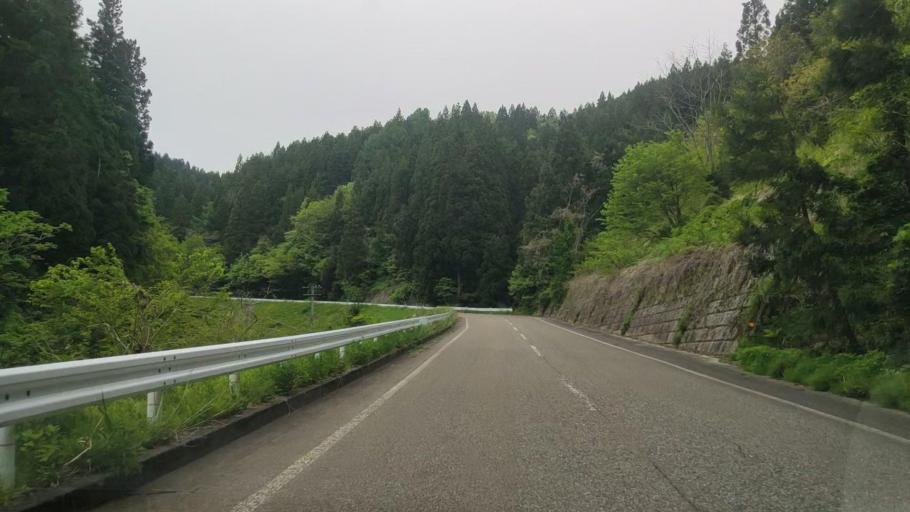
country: JP
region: Niigata
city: Gosen
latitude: 37.7143
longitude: 139.1177
